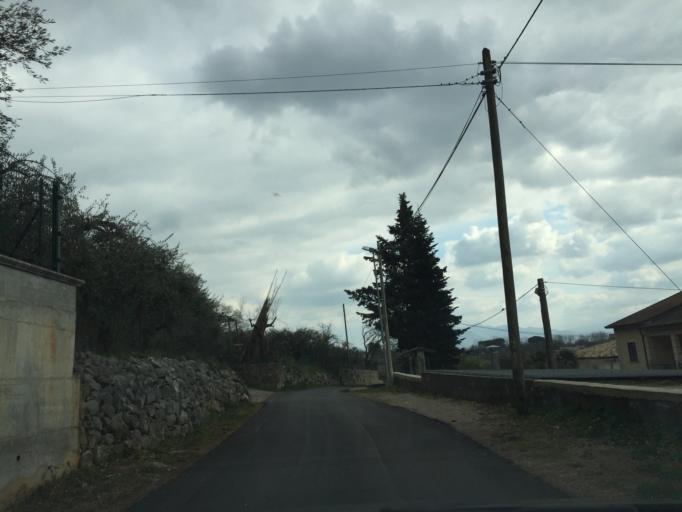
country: IT
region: Latium
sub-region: Provincia di Frosinone
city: Villa Santa Lucia
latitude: 41.4900
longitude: 13.7848
